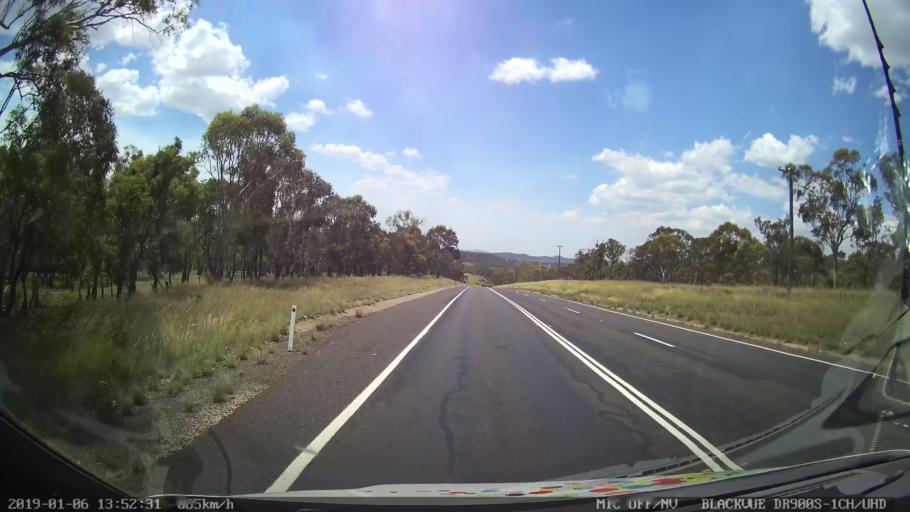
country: AU
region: New South Wales
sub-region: Tamworth Municipality
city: Kootingal
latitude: -30.9194
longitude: 151.1327
